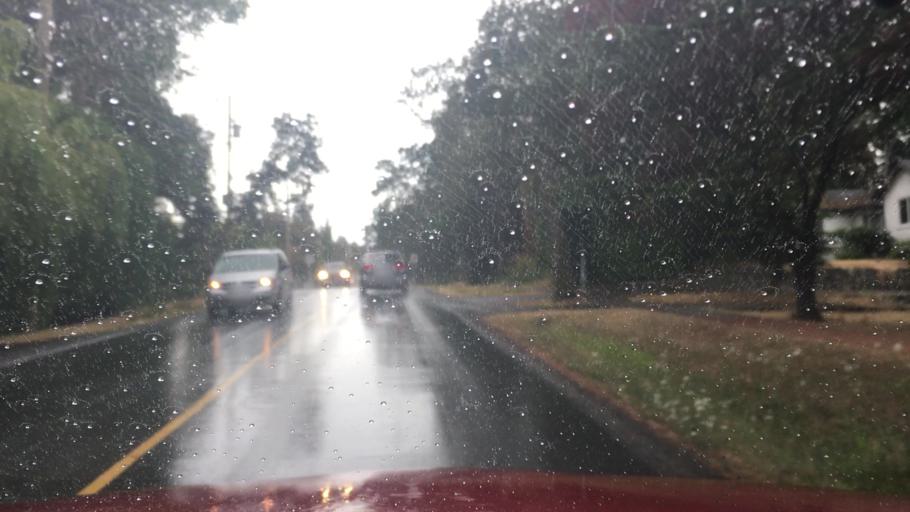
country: CA
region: British Columbia
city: Victoria
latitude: 48.4698
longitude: -123.3505
